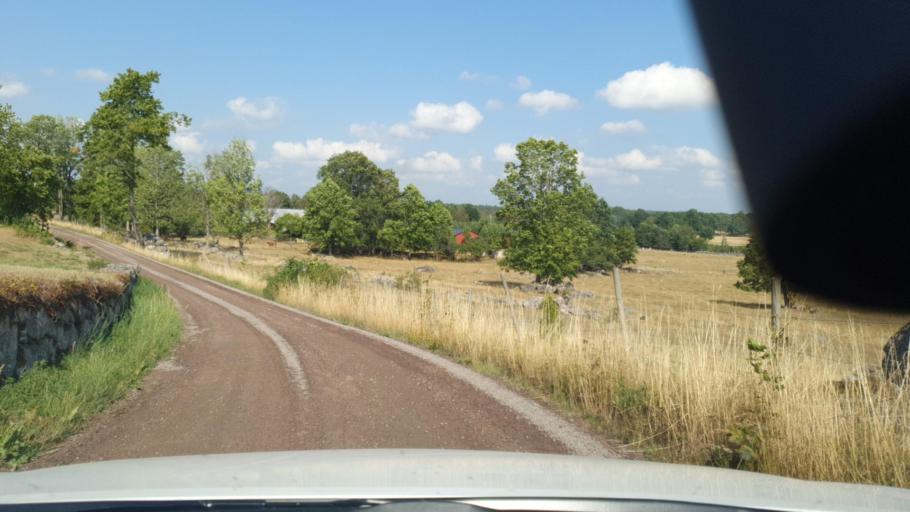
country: SE
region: Kalmar
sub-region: Hultsfreds Kommun
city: Malilla
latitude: 57.3143
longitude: 15.8161
